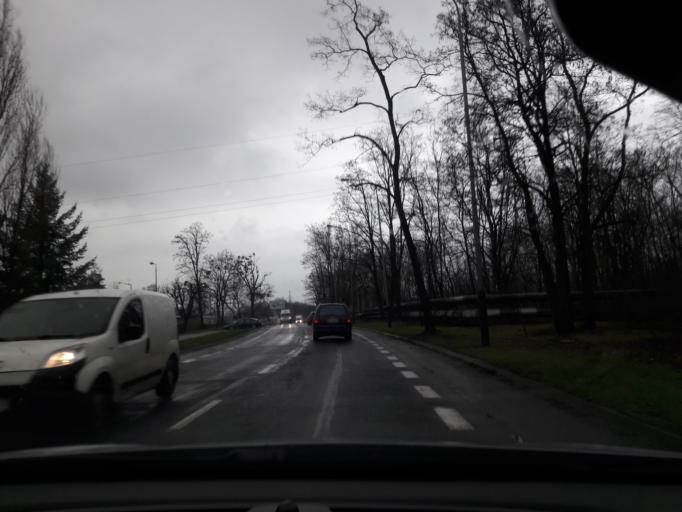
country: PL
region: Greater Poland Voivodeship
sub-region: Powiat poznanski
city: Suchy Las
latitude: 52.4446
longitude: 16.9017
